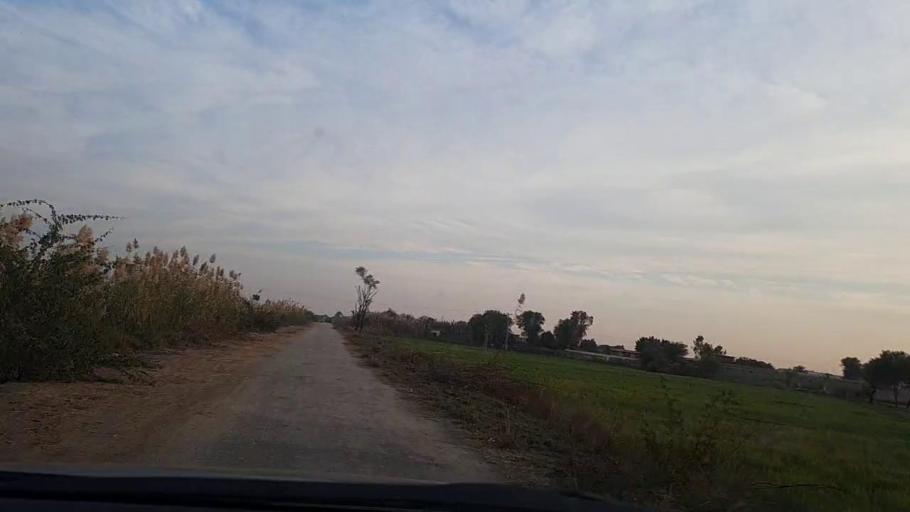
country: PK
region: Sindh
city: Sakrand
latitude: 26.1773
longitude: 68.3432
